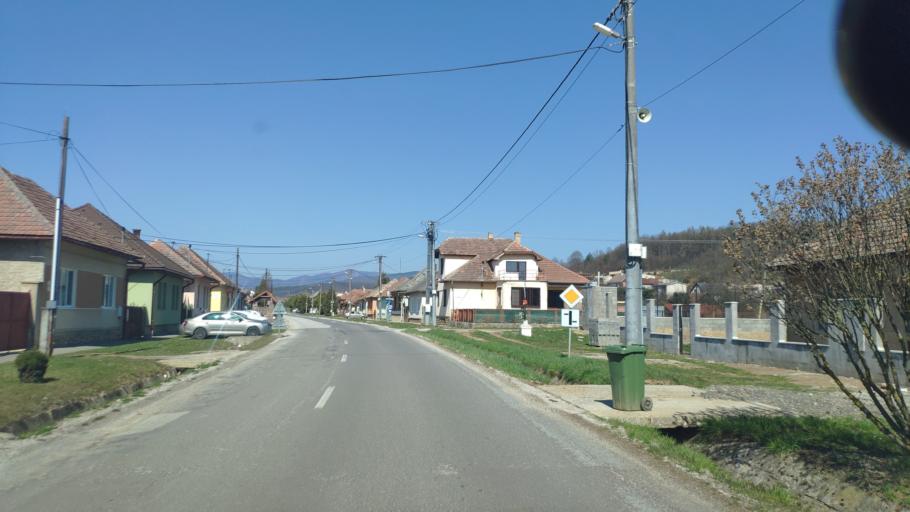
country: SK
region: Kosicky
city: Moldava nad Bodvou
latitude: 48.6777
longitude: 20.9822
